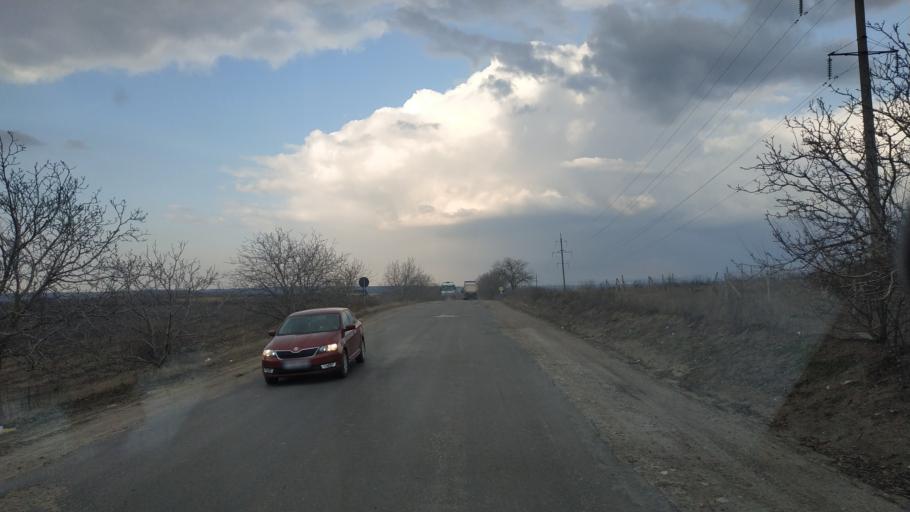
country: MD
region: Anenii Noi
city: Anenii Noi
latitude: 46.9633
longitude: 29.2846
